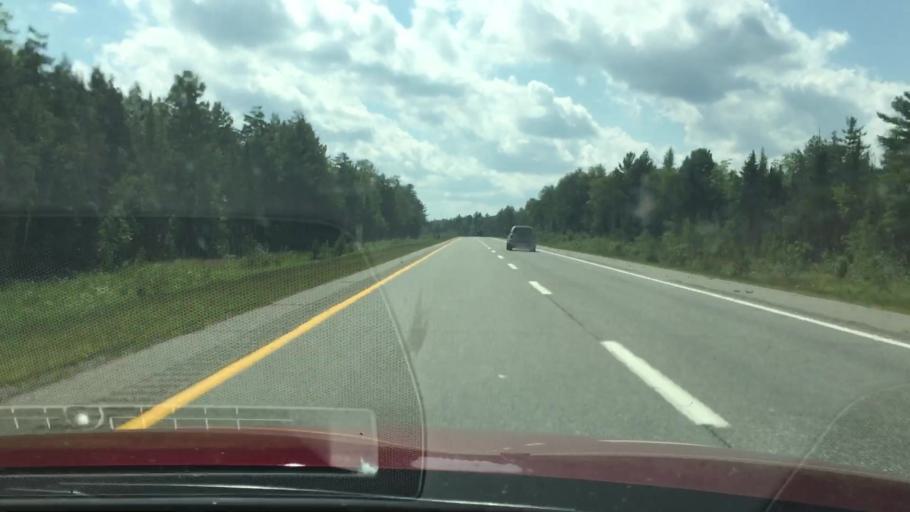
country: US
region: Maine
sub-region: Penobscot County
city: Howland
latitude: 45.3202
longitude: -68.6506
